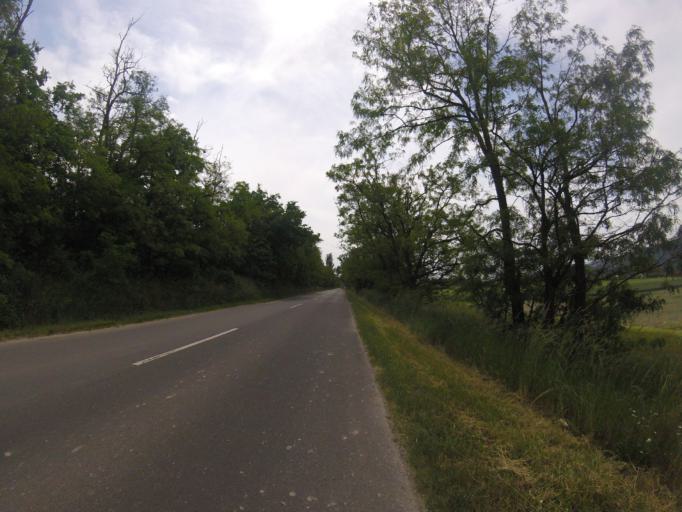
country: HU
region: Pest
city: Leanyfalu
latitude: 47.7244
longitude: 19.1043
